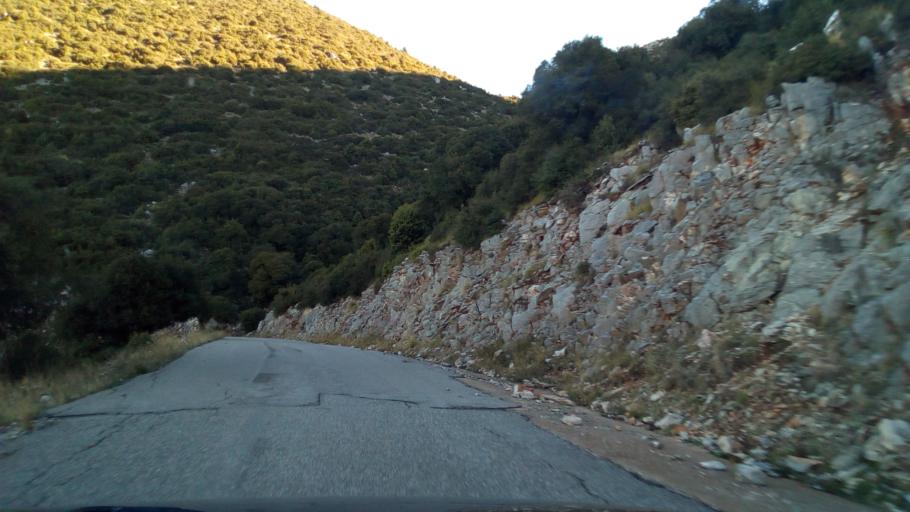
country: GR
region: West Greece
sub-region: Nomos Aitolias kai Akarnanias
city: Nafpaktos
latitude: 38.5185
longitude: 21.8499
